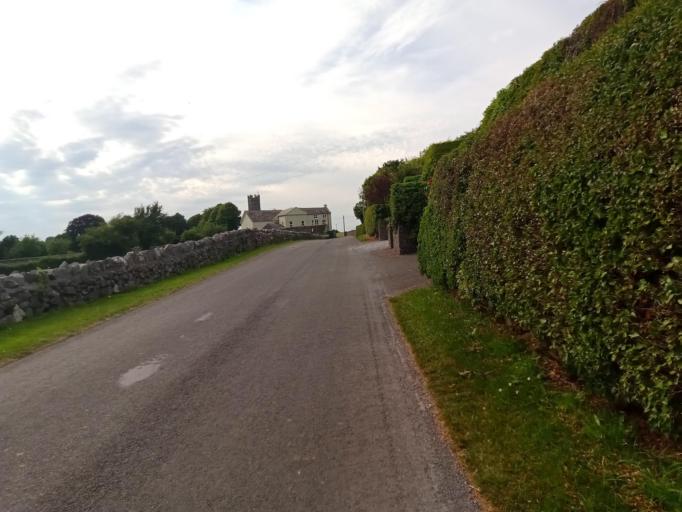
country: IE
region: Leinster
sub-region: Laois
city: Rathdowney
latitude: 52.8216
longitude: -7.4796
